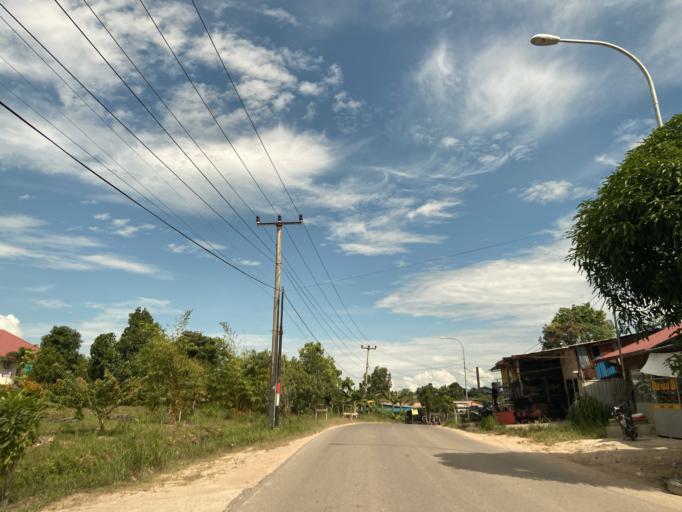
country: SG
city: Singapore
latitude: 1.0237
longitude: 103.9456
